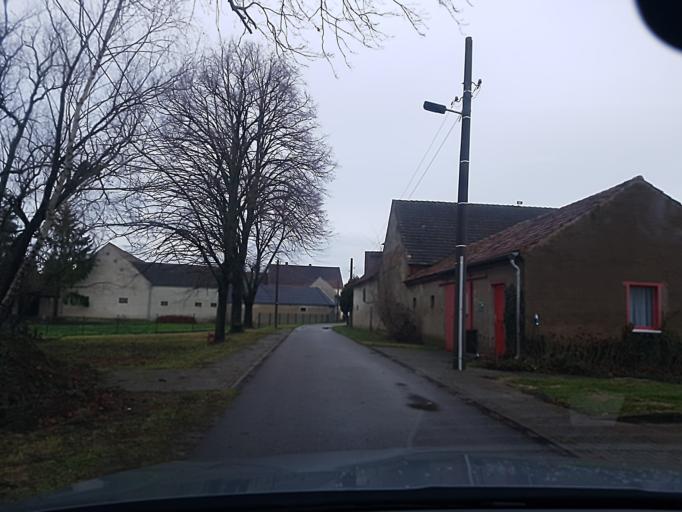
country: DE
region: Brandenburg
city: Falkenberg
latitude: 51.6127
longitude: 13.2933
